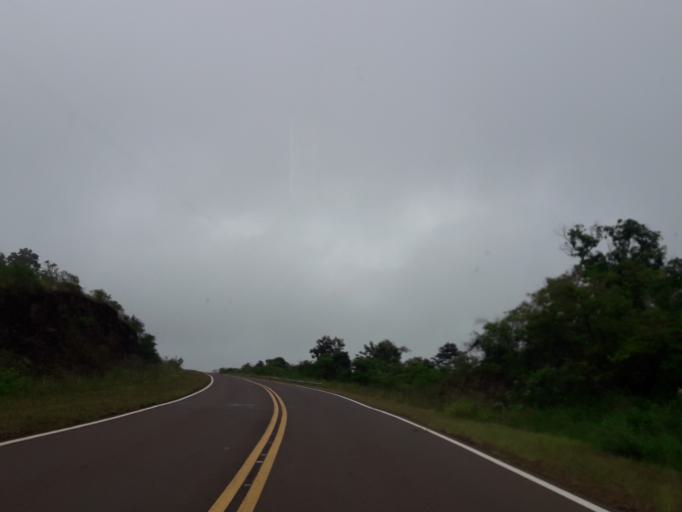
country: AR
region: Misiones
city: Bernardo de Irigoyen
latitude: -26.4095
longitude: -53.8234
